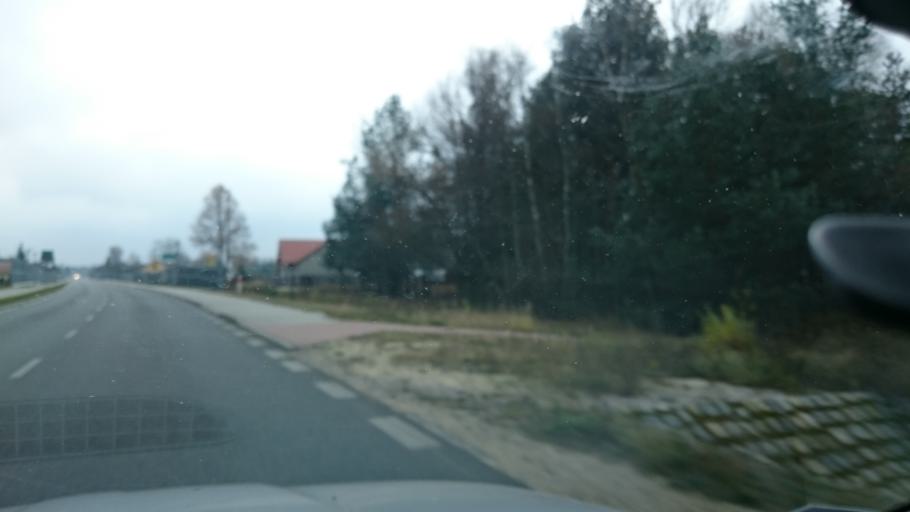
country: PL
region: Swietokrzyskie
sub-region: Powiat konecki
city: Konskie
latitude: 51.1491
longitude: 20.3618
